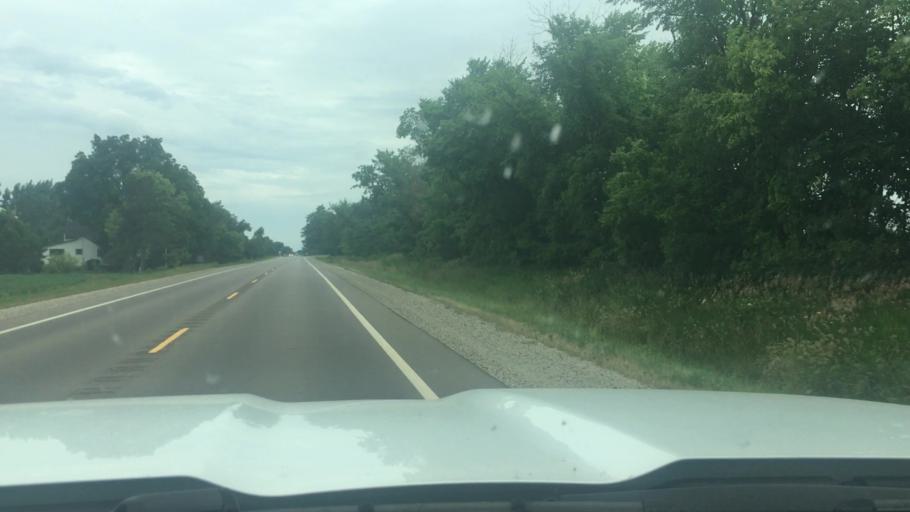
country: US
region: Michigan
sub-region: Clinton County
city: Saint Johns
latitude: 43.0017
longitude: -84.6330
